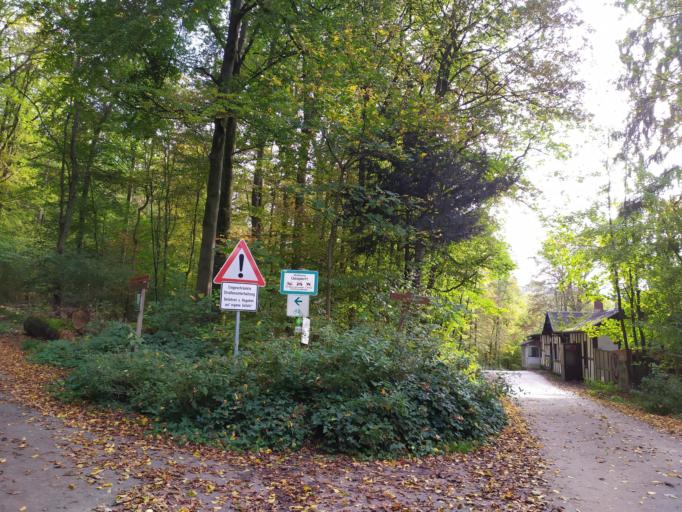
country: DE
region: Baden-Wuerttemberg
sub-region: Regierungsbezirk Stuttgart
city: Weinsberg
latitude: 49.1296
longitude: 9.2578
